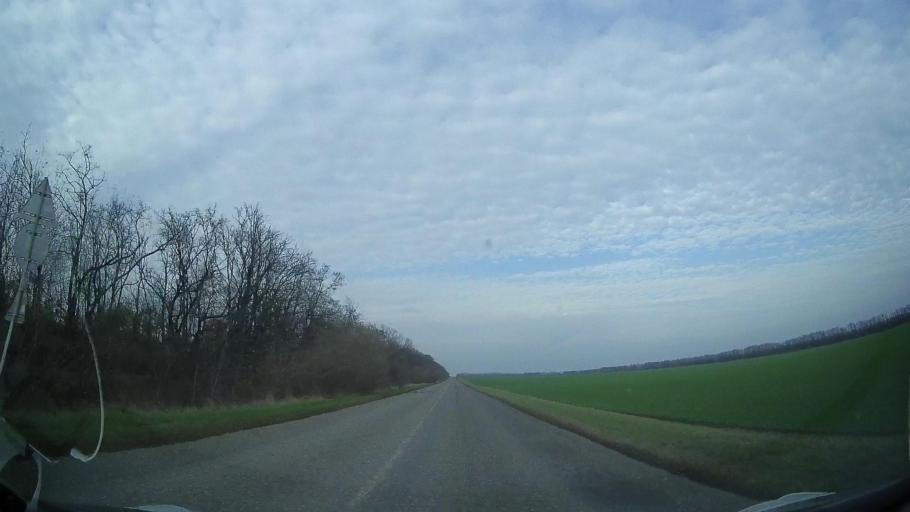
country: RU
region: Rostov
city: Zernograd
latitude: 46.9691
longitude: 40.3916
